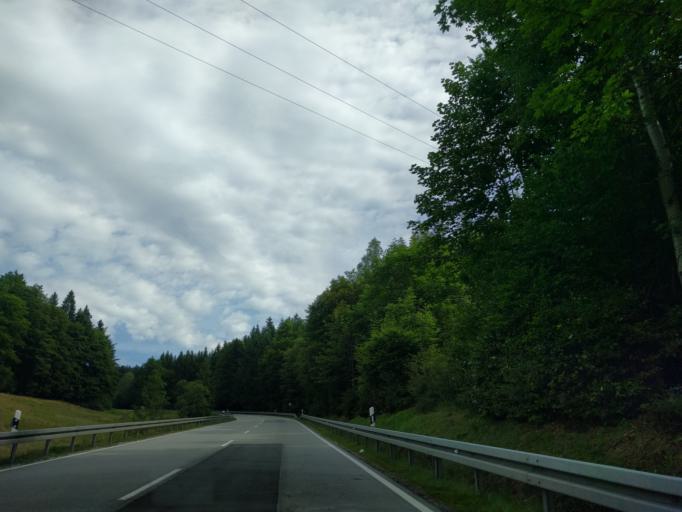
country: DE
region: Bavaria
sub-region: Lower Bavaria
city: Schaufling
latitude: 48.8729
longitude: 13.0484
